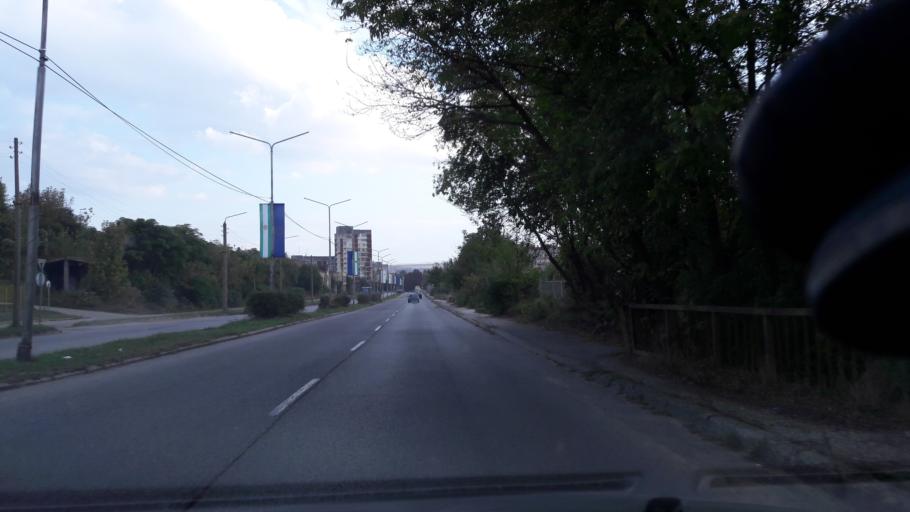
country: BG
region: Razgrad
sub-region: Obshtina Razgrad
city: Razgrad
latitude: 43.5370
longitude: 26.5199
